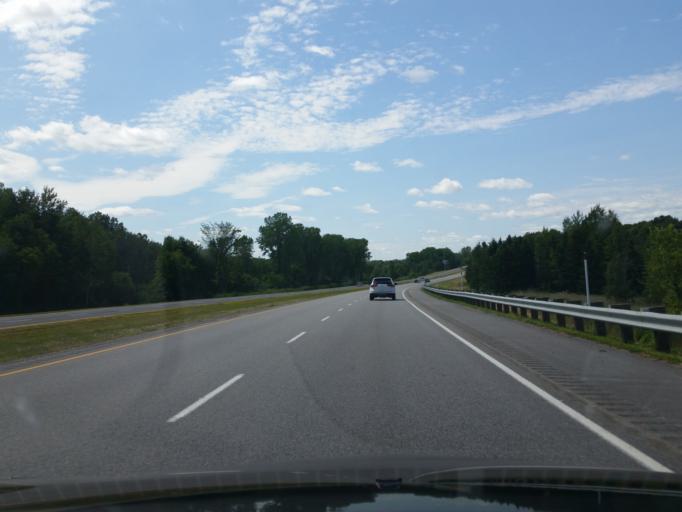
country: CA
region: Quebec
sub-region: Monteregie
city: Hudson
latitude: 45.4395
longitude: -74.1909
